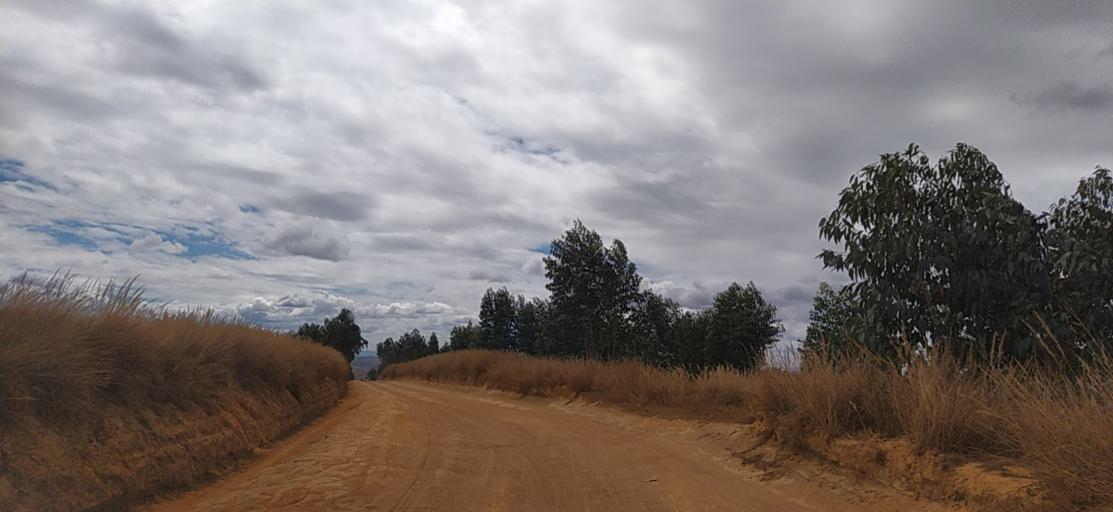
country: MG
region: Alaotra Mangoro
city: Ambatondrazaka
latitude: -17.9926
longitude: 48.2655
